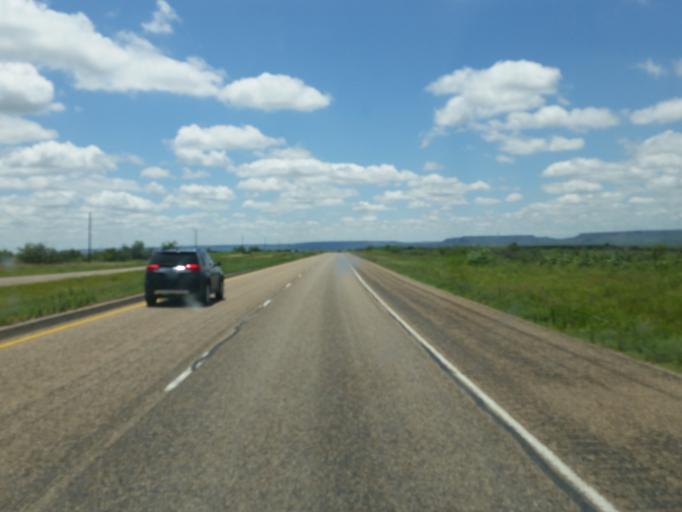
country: US
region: Texas
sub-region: Garza County
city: Post
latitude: 33.0879
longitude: -101.2436
